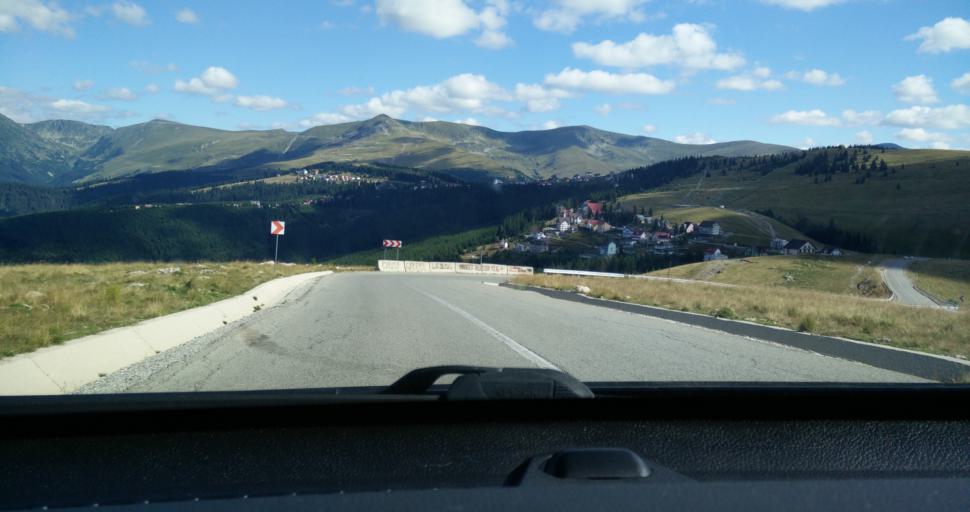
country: RO
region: Gorj
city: Novaci-Straini
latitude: 45.2691
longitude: 23.6839
